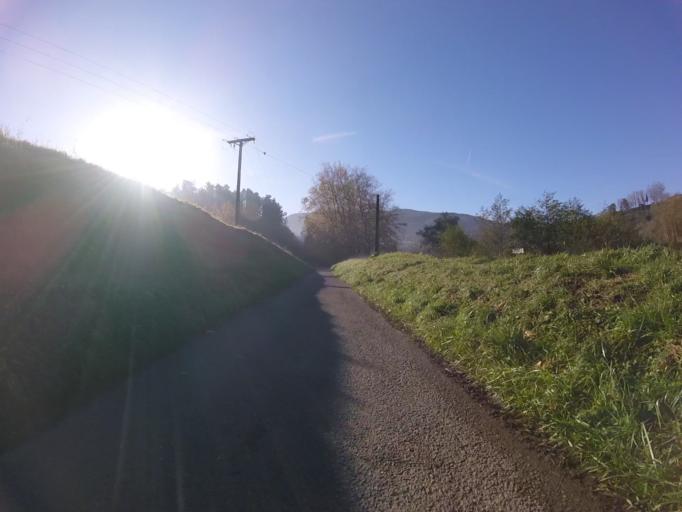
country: ES
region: Basque Country
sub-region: Provincia de Guipuzcoa
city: Usurbil
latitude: 43.2749
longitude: -2.0651
